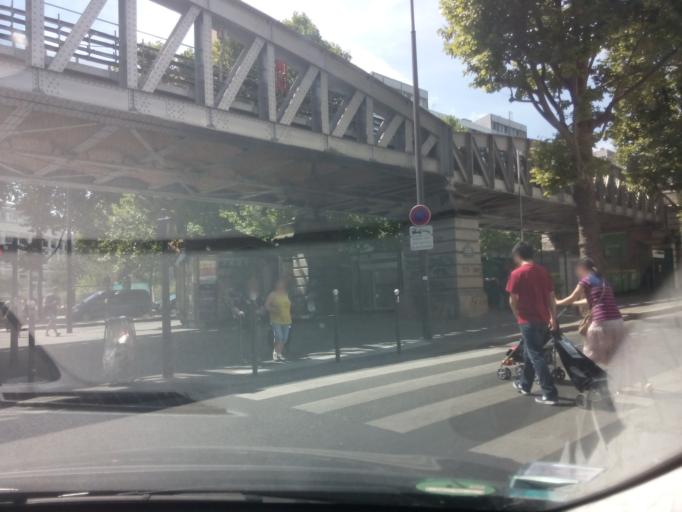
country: FR
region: Ile-de-France
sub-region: Departement du Val-de-Marne
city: Le Kremlin-Bicetre
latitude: 48.8332
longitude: 2.3617
